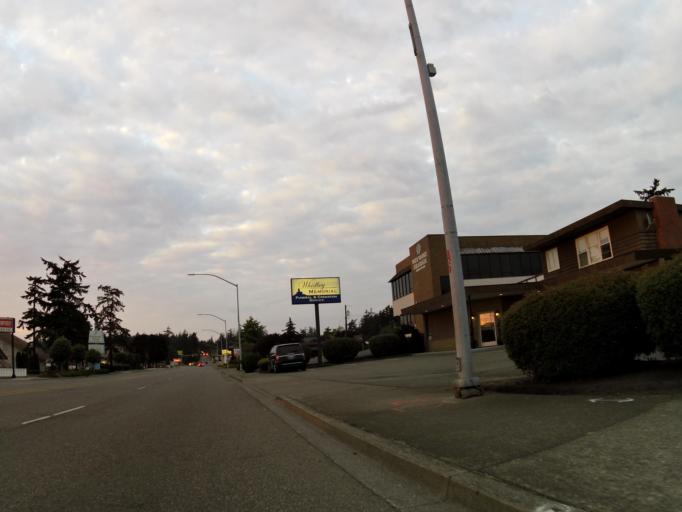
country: US
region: Washington
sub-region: Island County
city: Oak Harbor
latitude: 48.3040
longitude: -122.6432
